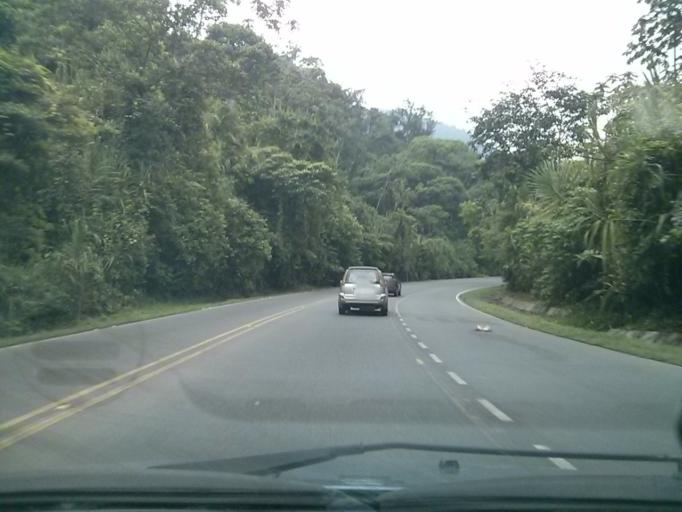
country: CR
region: San Jose
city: Dulce Nombre de Jesus
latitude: 10.1651
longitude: -83.9364
